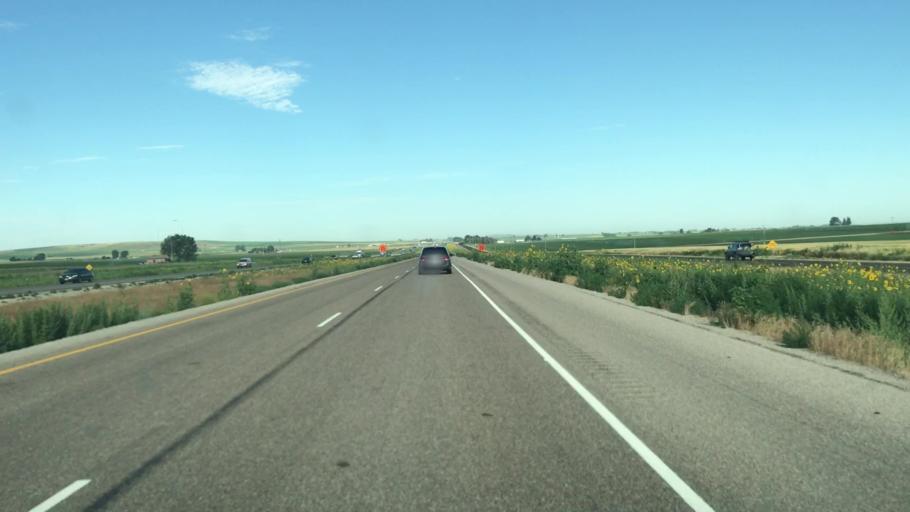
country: US
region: Idaho
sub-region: Cassia County
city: Burley
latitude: 42.5764
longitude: -114.0239
